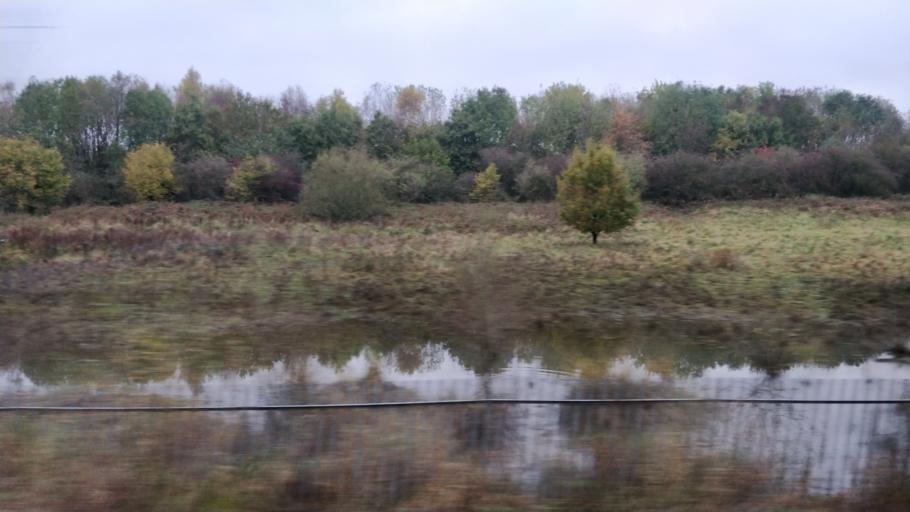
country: GB
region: England
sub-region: Borough of Wigan
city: Tyldesley
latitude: 53.5286
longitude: -2.4690
